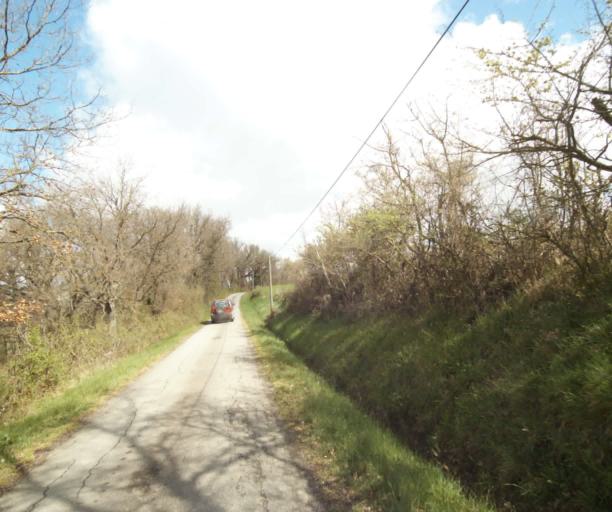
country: FR
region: Midi-Pyrenees
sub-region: Departement de l'Ariege
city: Saverdun
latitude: 43.2016
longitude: 1.5812
